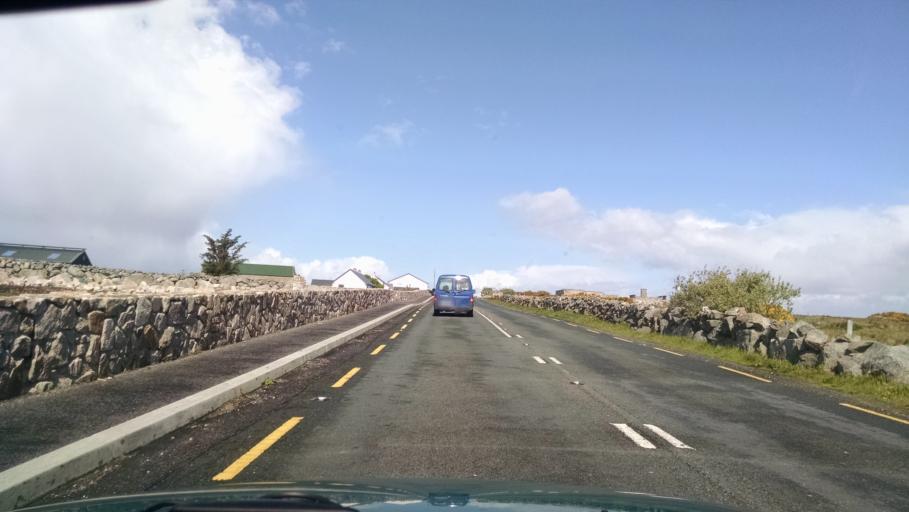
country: IE
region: Connaught
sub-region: County Galway
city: Oughterard
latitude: 53.2399
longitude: -9.4994
